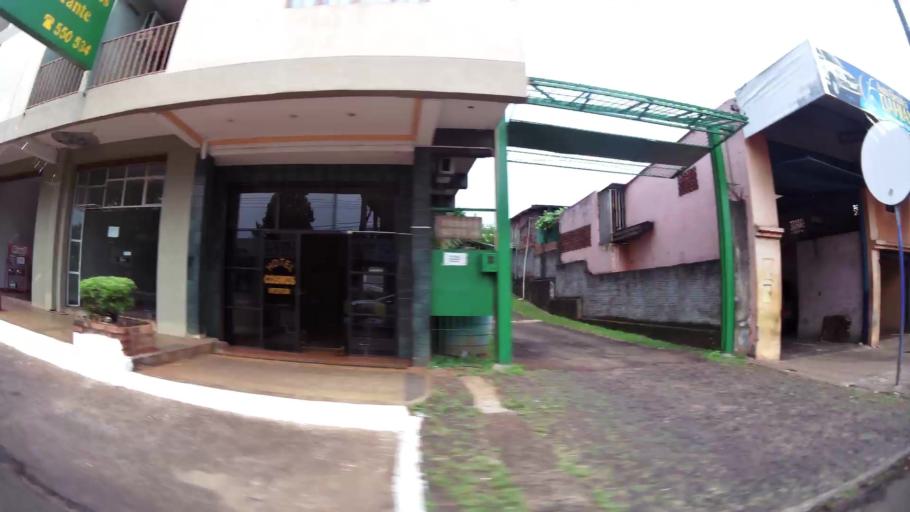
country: BR
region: Parana
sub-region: Foz Do Iguacu
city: Foz do Iguacu
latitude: -25.5563
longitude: -54.6068
